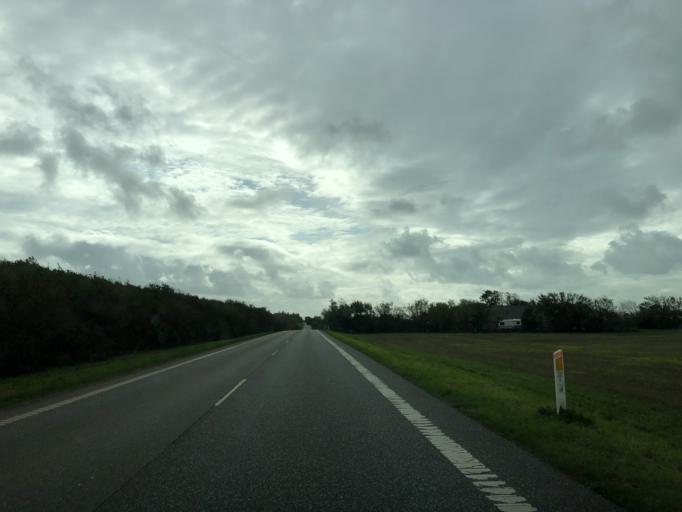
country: DK
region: North Denmark
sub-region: Thisted Kommune
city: Hurup
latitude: 56.7197
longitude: 8.4207
